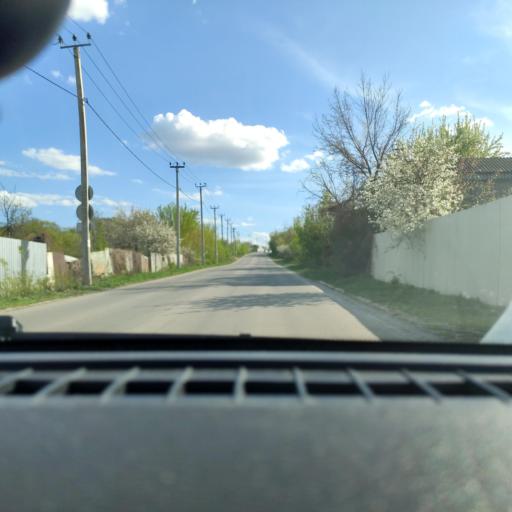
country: RU
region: Samara
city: Zhigulevsk
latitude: 53.3776
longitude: 49.4950
